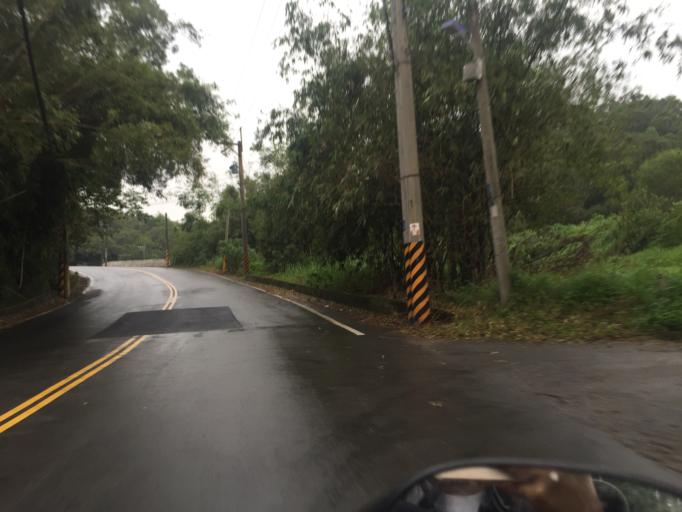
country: TW
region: Taiwan
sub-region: Hsinchu
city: Hsinchu
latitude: 24.7693
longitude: 120.9473
